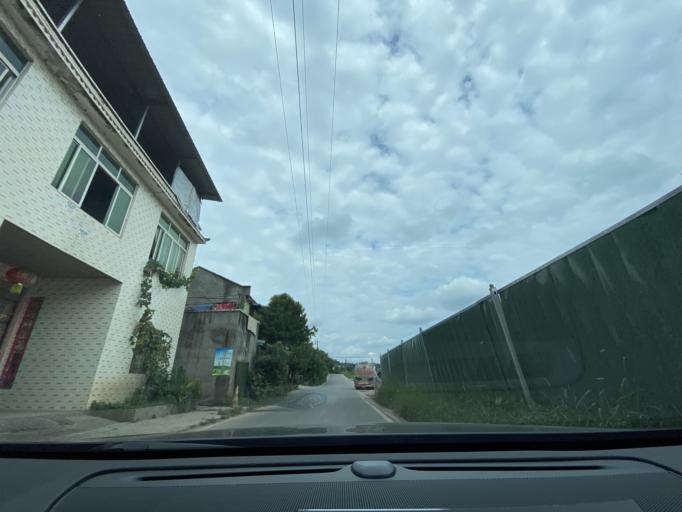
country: CN
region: Sichuan
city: Jiancheng
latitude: 30.4356
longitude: 104.5277
